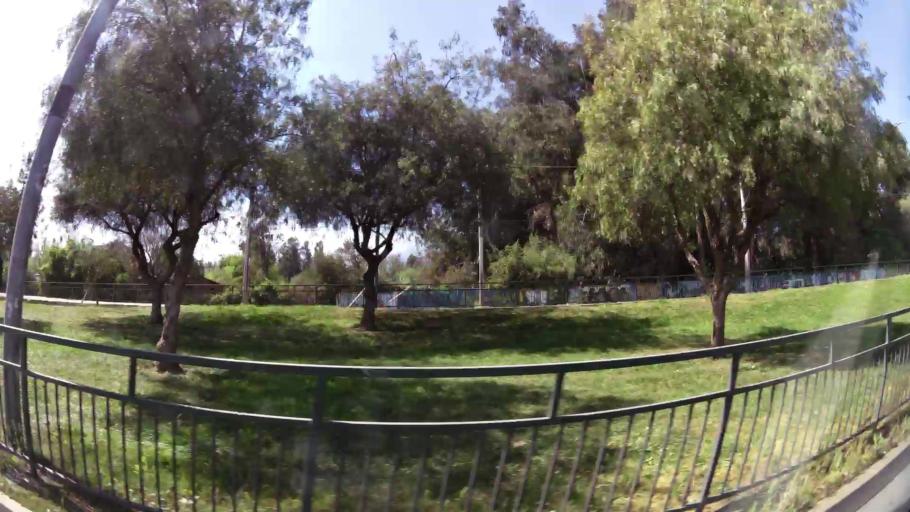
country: CL
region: Santiago Metropolitan
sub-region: Provincia de Cordillera
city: Puente Alto
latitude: -33.5810
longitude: -70.5502
